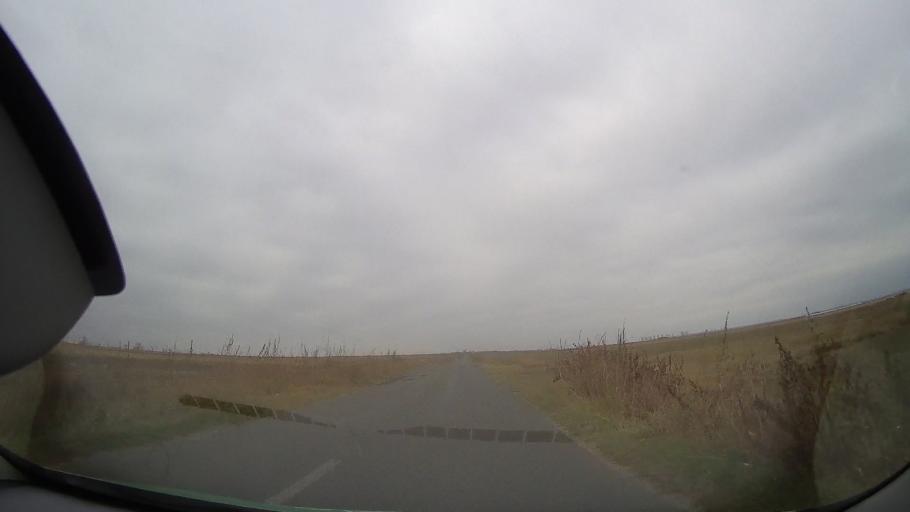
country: RO
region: Buzau
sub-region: Comuna Luciu
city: Luciu
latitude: 44.9757
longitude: 27.0630
